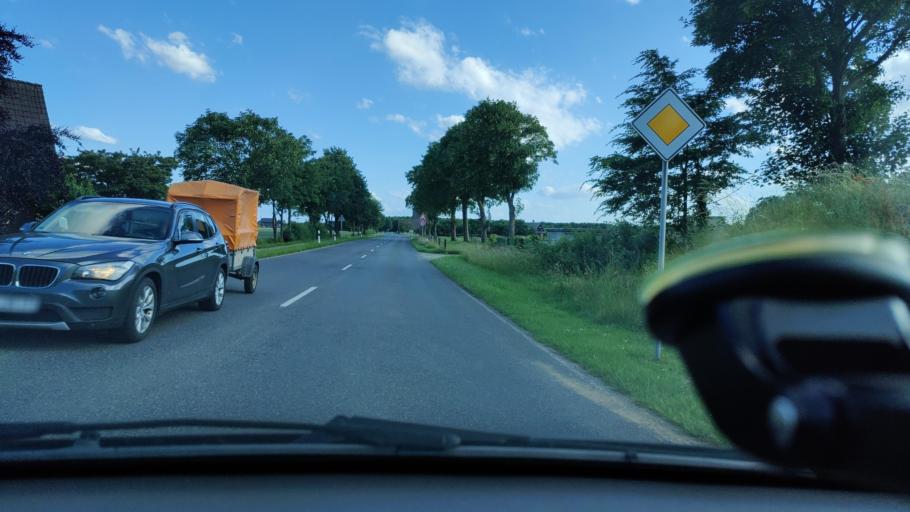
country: DE
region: North Rhine-Westphalia
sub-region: Regierungsbezirk Dusseldorf
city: Alpen
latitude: 51.5540
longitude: 6.5308
